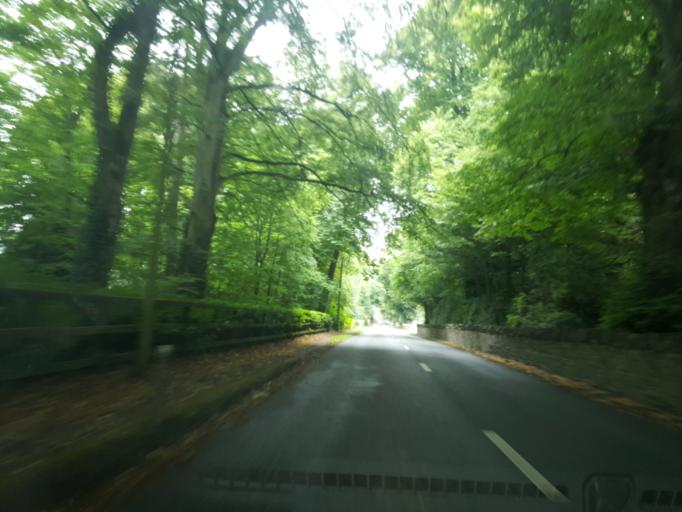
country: IE
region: Leinster
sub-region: Kildare
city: Kilcullen
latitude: 53.1219
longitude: -6.7020
